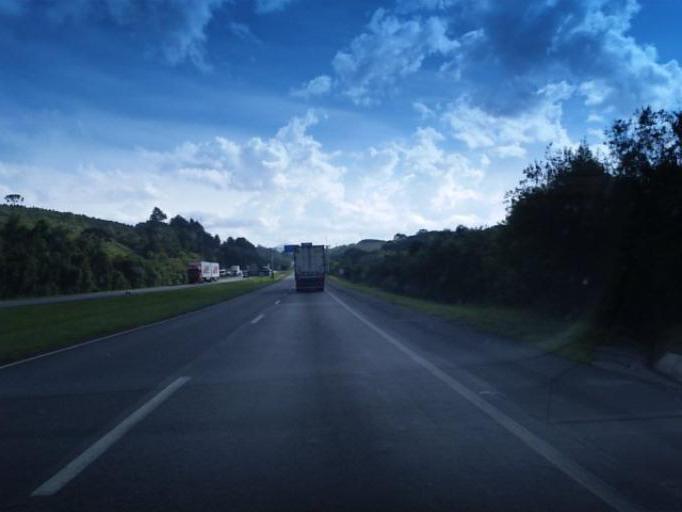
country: BR
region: Parana
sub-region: Campina Grande Do Sul
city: Campina Grande do Sul
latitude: -25.2778
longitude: -48.9249
